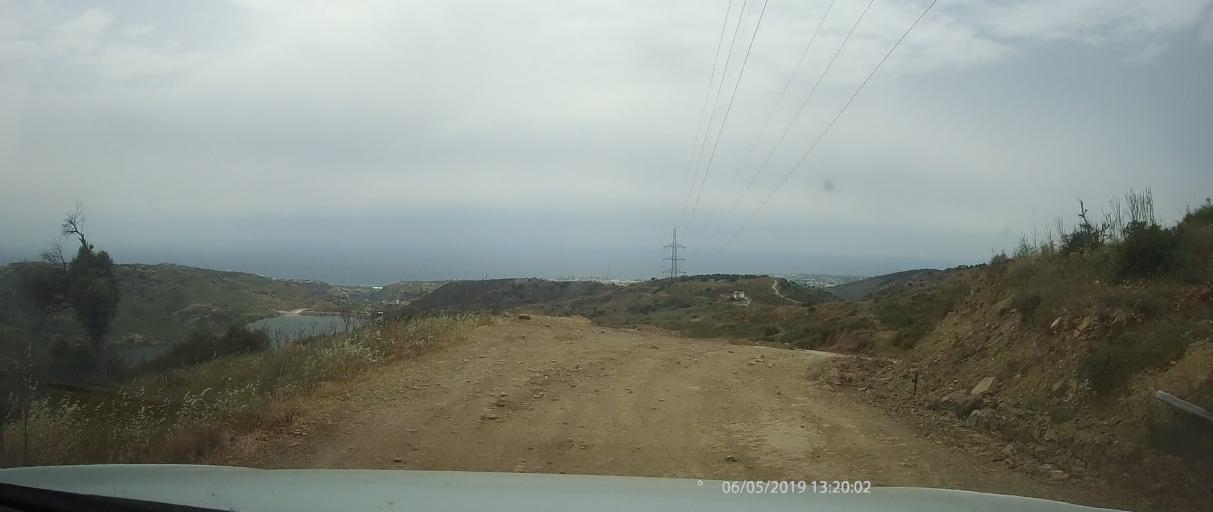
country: CY
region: Pafos
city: Tala
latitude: 34.8652
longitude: 32.4178
